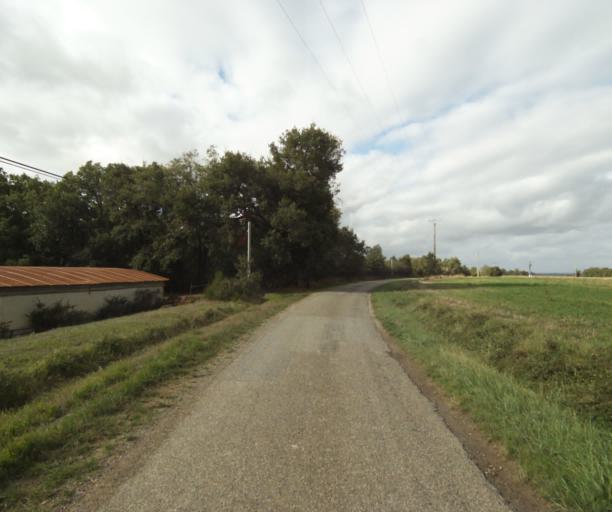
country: FR
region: Midi-Pyrenees
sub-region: Departement du Tarn-et-Garonne
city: Beaumont-de-Lomagne
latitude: 43.8852
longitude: 1.0824
